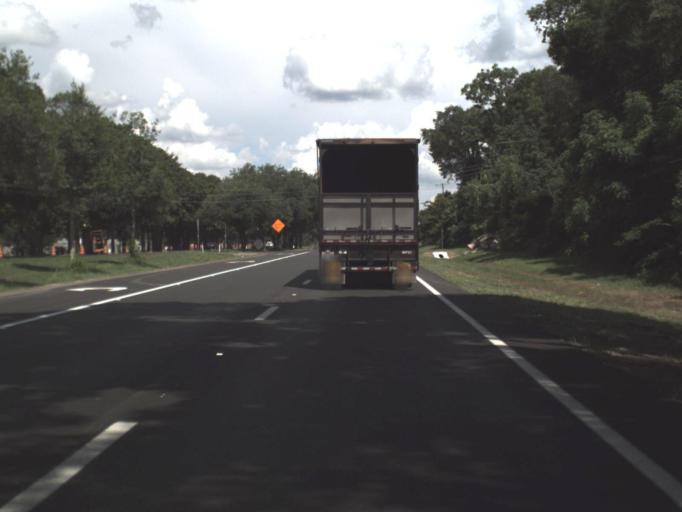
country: US
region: Florida
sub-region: Alachua County
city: Alachua
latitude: 29.7743
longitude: -82.4403
